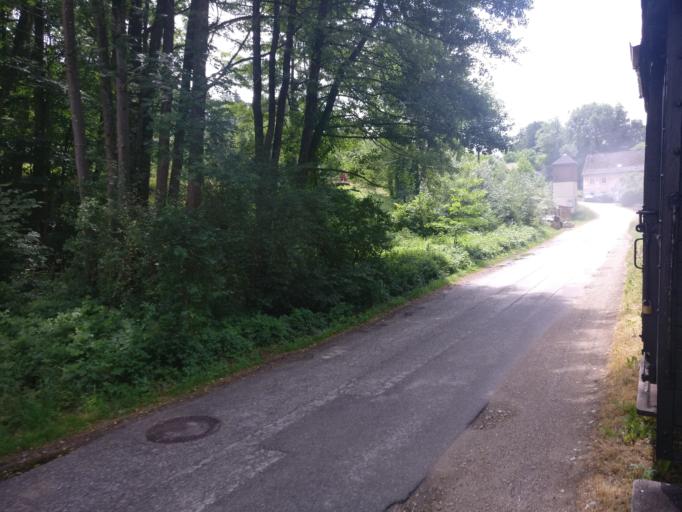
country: AT
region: Upper Austria
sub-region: Politischer Bezirk Steyr-Land
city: Sierning
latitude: 48.0305
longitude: 14.3372
